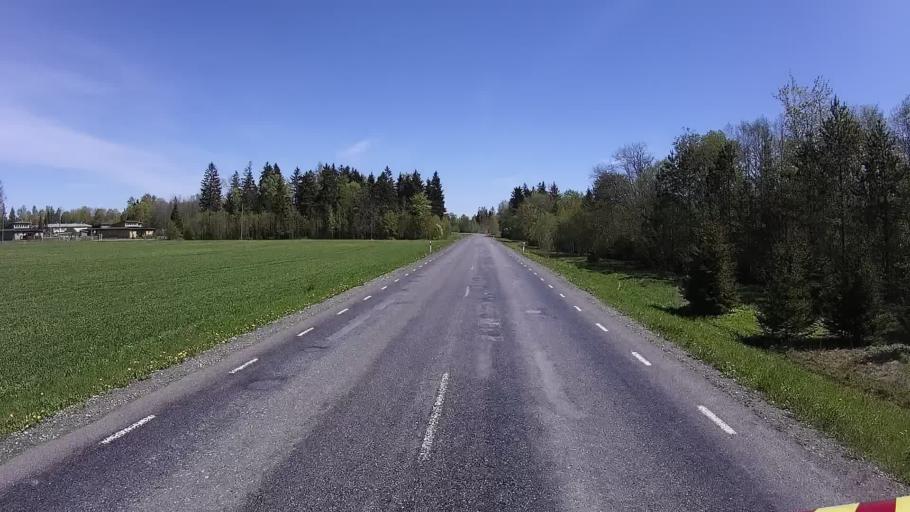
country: EE
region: Raplamaa
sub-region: Kehtna vald
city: Kehtna
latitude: 59.0544
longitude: 24.9593
